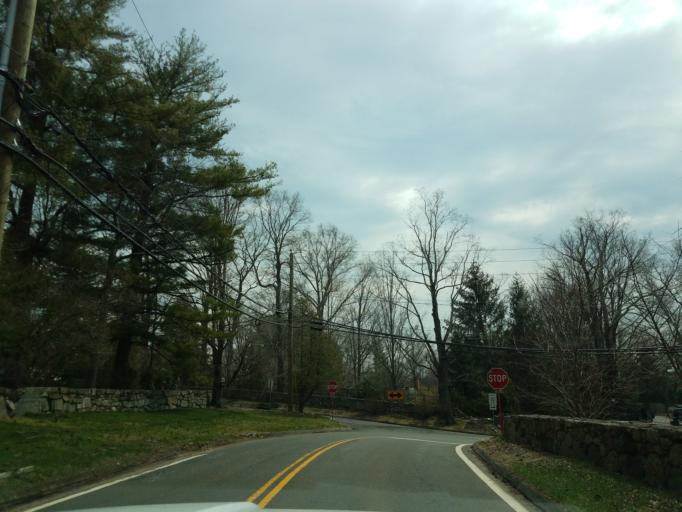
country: US
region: Connecticut
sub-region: Fairfield County
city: Glenville
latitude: 41.0911
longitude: -73.6477
